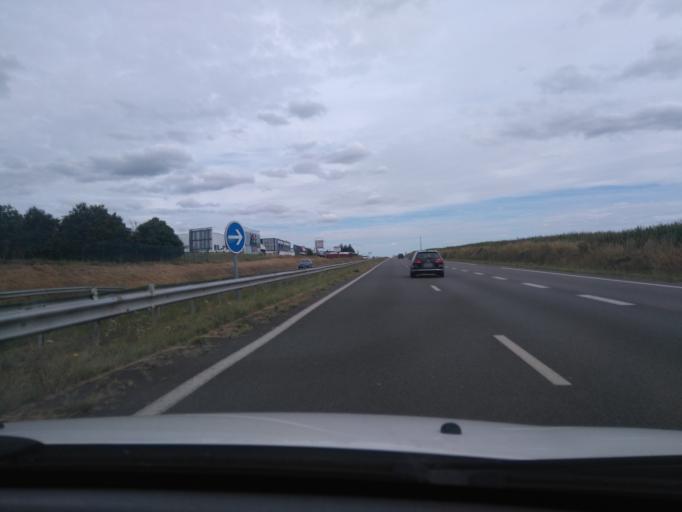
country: FR
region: Brittany
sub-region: Departement des Cotes-d'Armor
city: Plenee-Jugon
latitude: 48.3752
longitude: -2.3575
